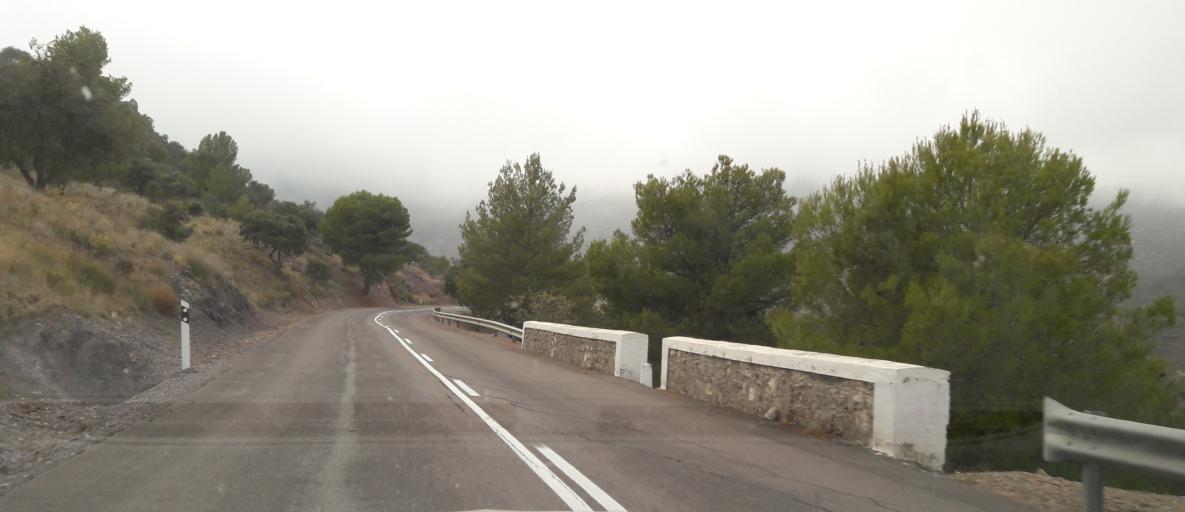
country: ES
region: Andalusia
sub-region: Provincia de Almeria
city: Enix
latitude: 36.8928
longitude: -2.6151
